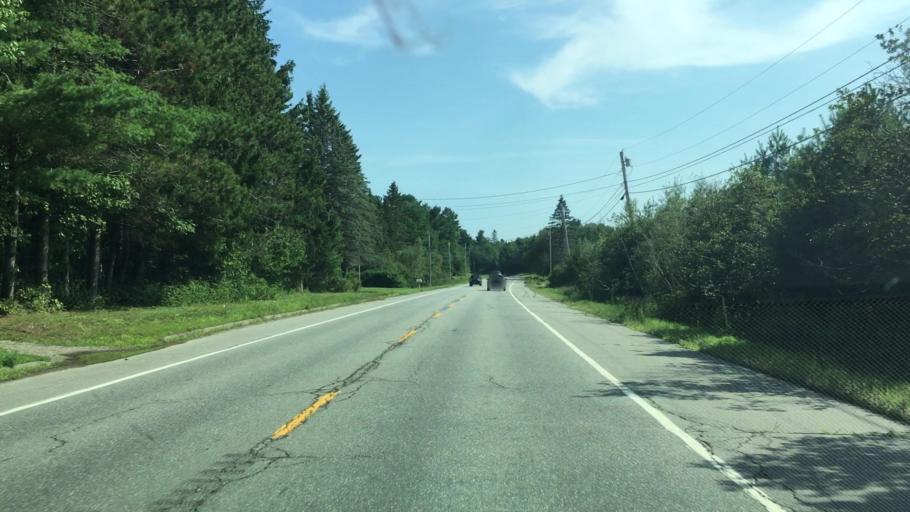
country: US
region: Maine
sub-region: Waldo County
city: Winterport
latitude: 44.6851
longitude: -68.8452
